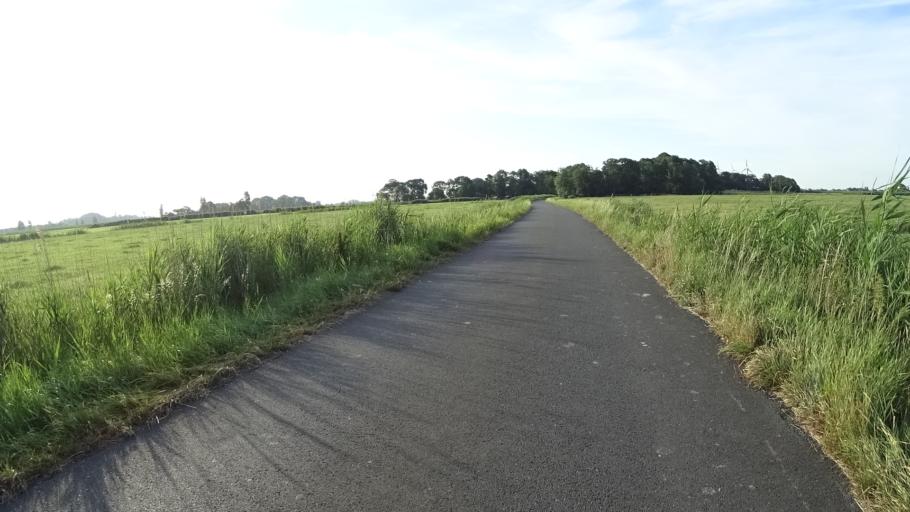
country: DE
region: Lower Saxony
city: Butjadingen
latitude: 53.6018
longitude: 8.2821
